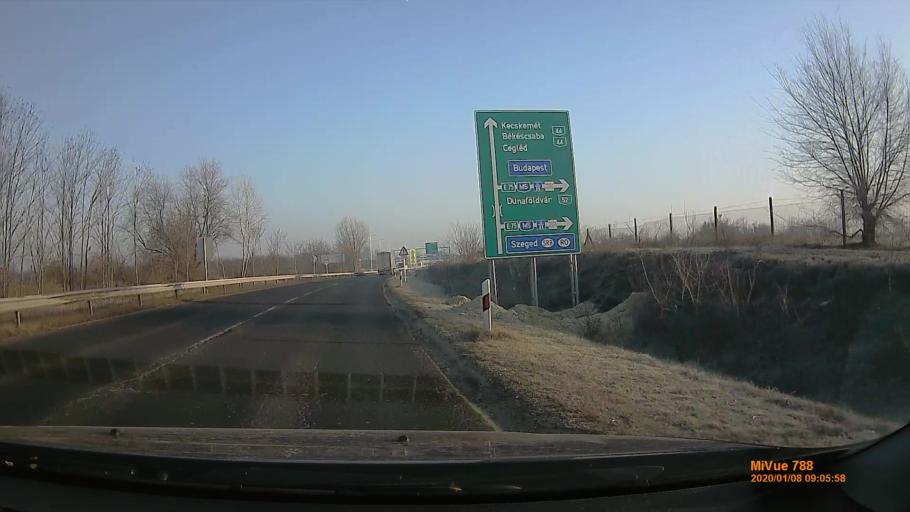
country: HU
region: Bacs-Kiskun
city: Helvecia
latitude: 46.8468
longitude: 19.6586
